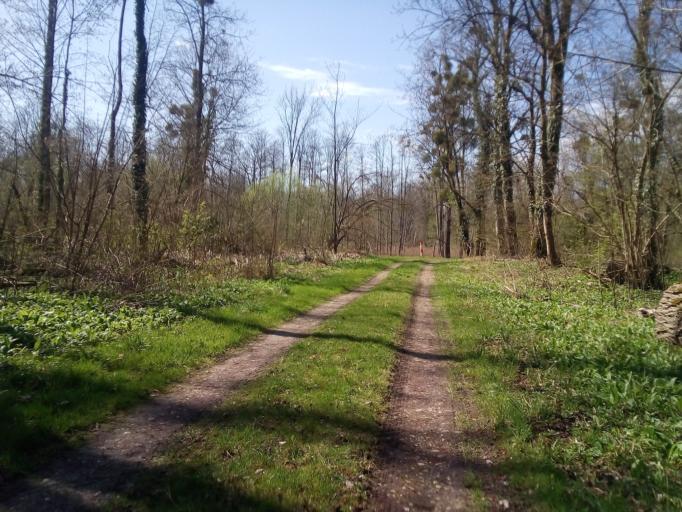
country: DE
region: Baden-Wuerttemberg
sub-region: Freiburg Region
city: Rheinau
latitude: 48.6890
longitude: 7.9479
